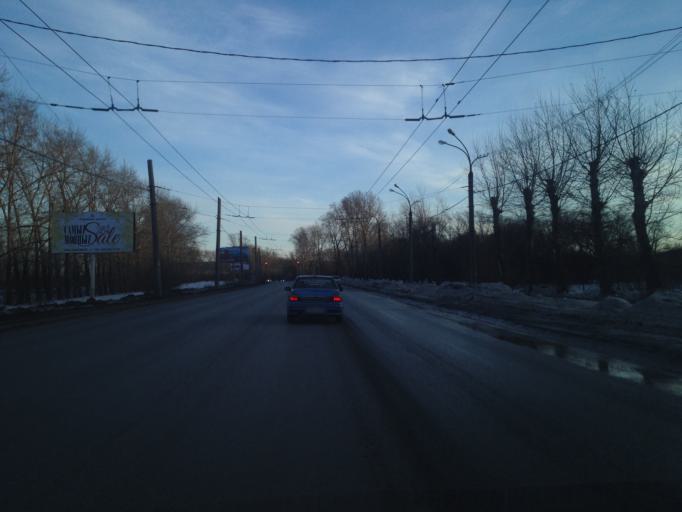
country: RU
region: Sverdlovsk
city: Yekaterinburg
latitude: 56.7675
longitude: 60.6706
